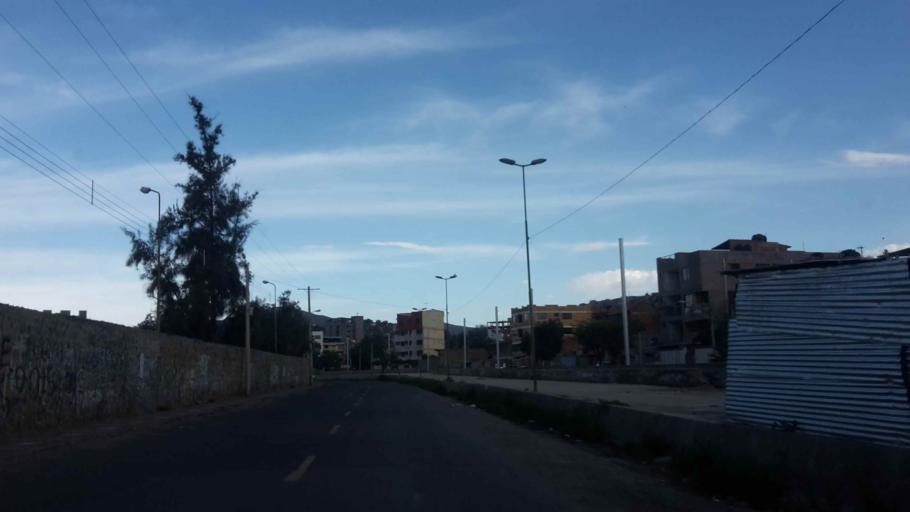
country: BO
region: Cochabamba
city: Cochabamba
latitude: -17.4108
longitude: -66.1609
